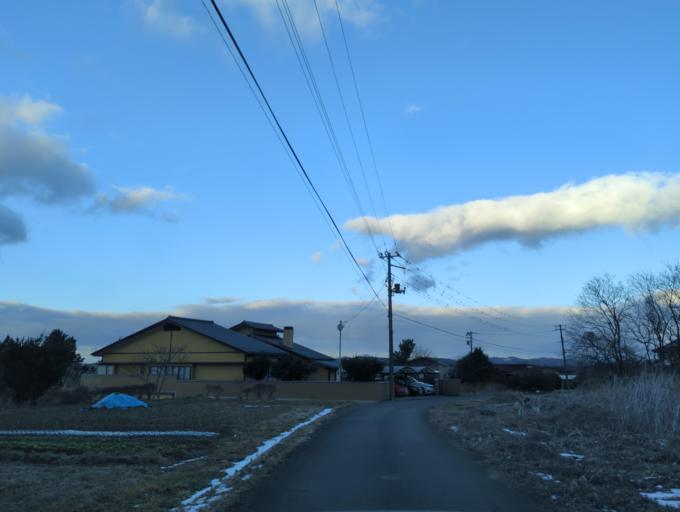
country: JP
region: Fukushima
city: Koriyama
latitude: 37.4482
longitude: 140.4003
